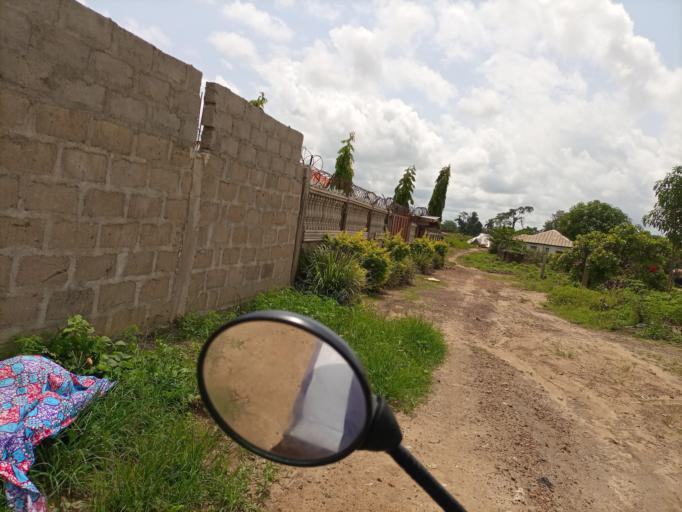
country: SL
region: Southern Province
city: Bo
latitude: 7.9800
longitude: -11.7686
